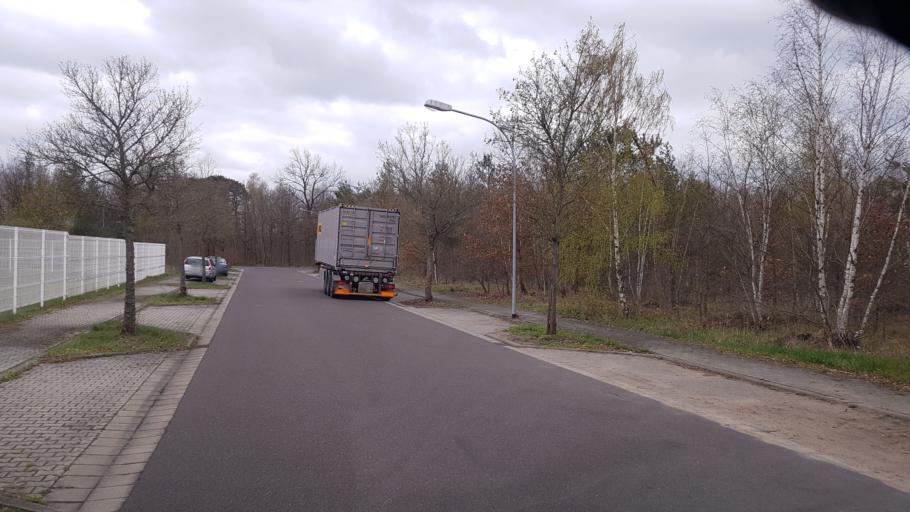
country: DE
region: Brandenburg
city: Schwarzheide
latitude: 51.4716
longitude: 13.8098
